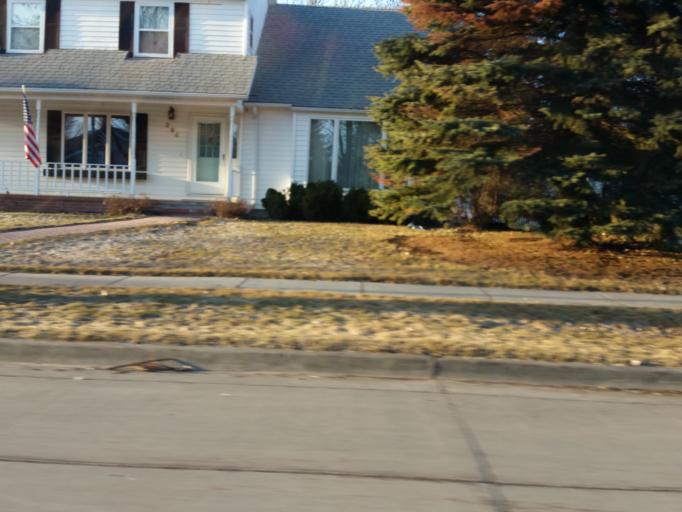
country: US
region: North Dakota
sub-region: Grand Forks County
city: Grand Forks
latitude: 47.8764
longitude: -97.0283
